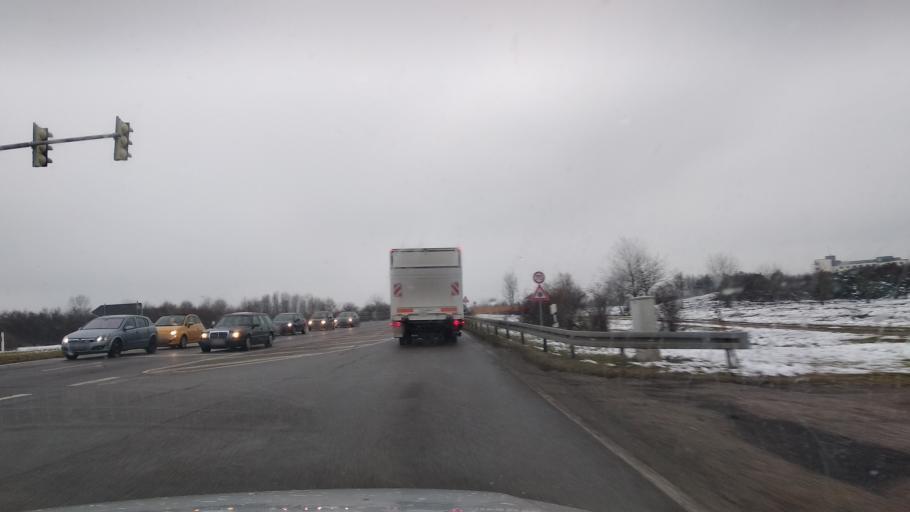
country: DE
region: Bavaria
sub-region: Upper Bavaria
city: Feldkirchen
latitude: 48.1446
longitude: 11.7453
